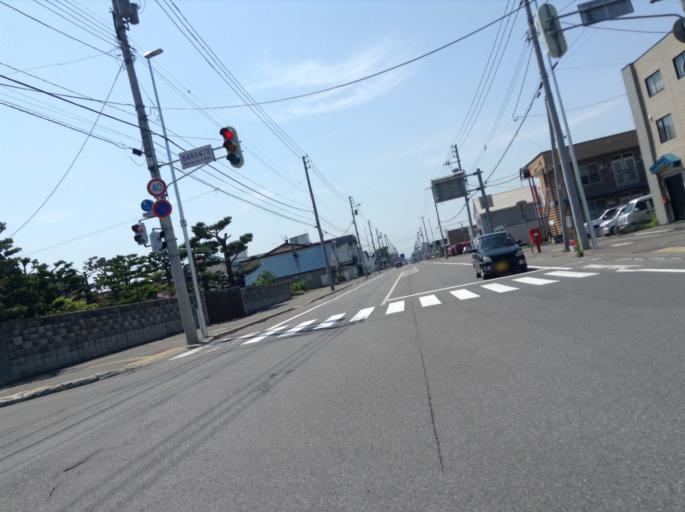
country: JP
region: Hokkaido
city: Nayoro
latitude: 44.3613
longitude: 142.4571
